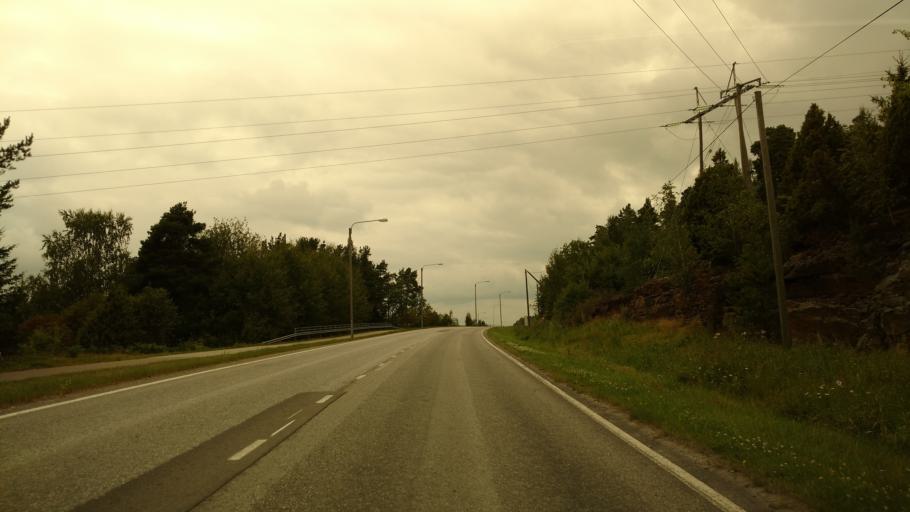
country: FI
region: Varsinais-Suomi
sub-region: Salo
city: Halikko
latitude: 60.4110
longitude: 23.0567
